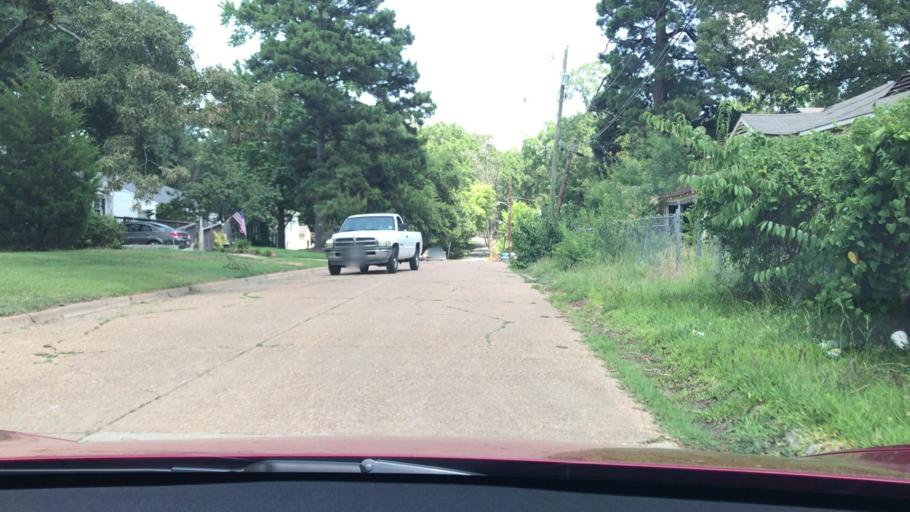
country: US
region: Louisiana
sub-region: Bossier Parish
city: Bossier City
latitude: 32.4946
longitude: -93.7284
